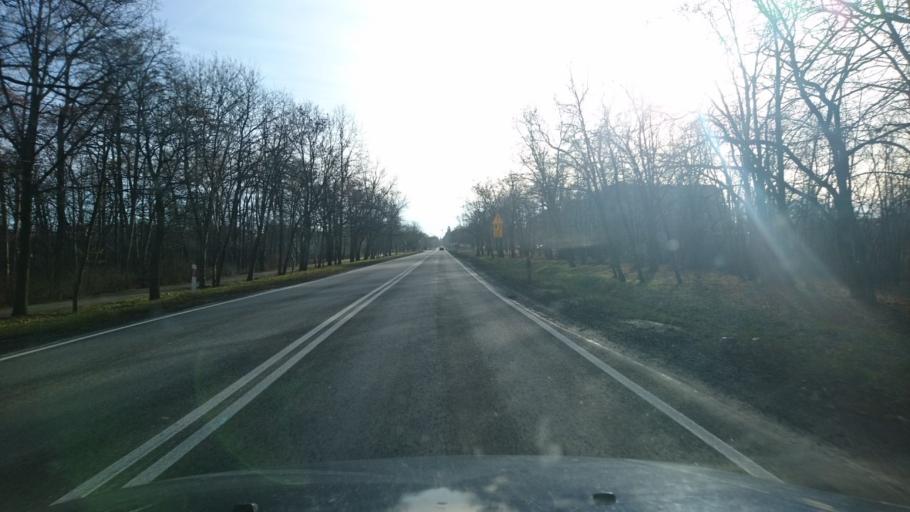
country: PL
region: Greater Poland Voivodeship
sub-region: Powiat ostrzeszowski
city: Ostrzeszow
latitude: 51.4335
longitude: 17.9169
